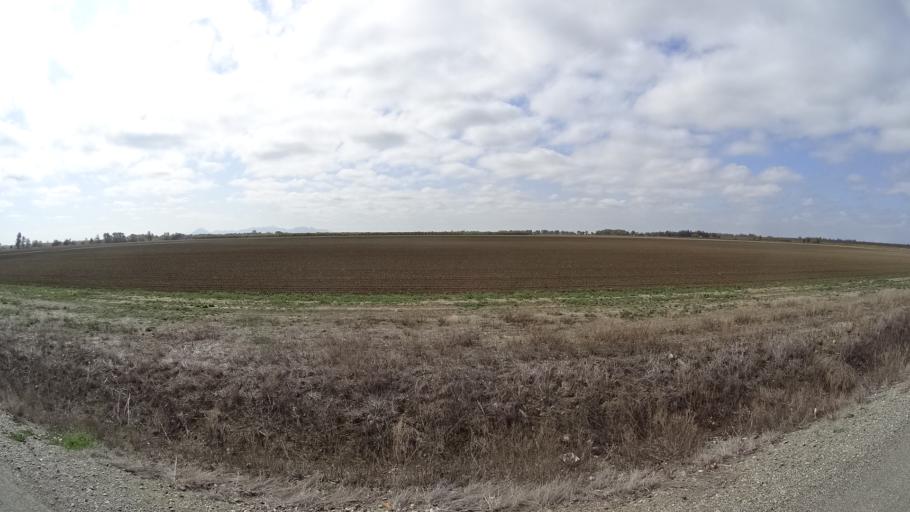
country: US
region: California
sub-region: Butte County
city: Biggs
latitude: 39.4203
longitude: -121.9270
